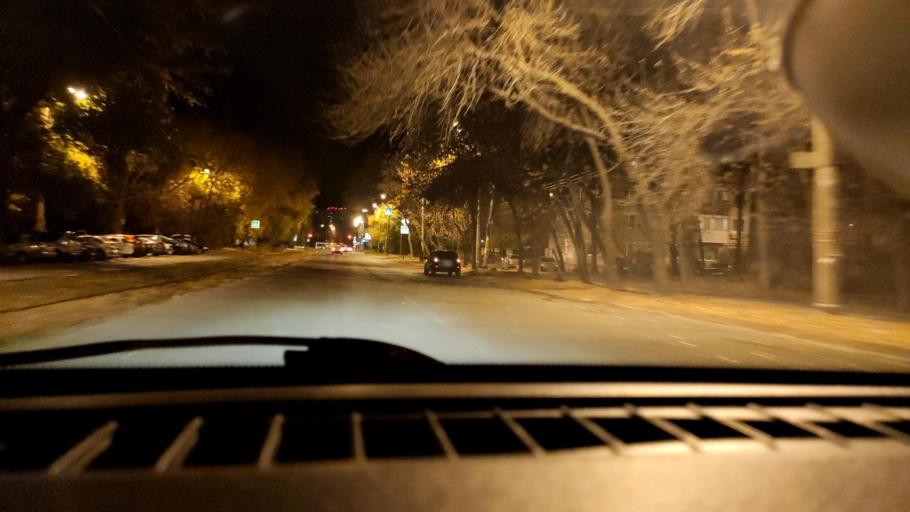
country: RU
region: Samara
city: Samara
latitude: 53.2106
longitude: 50.1830
